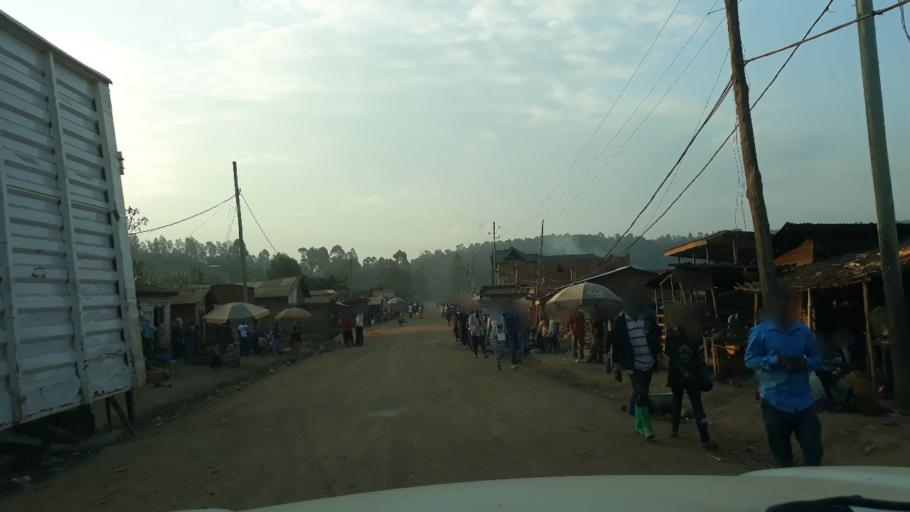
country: CD
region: South Kivu
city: Bukavu
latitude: -2.6601
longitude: 28.8741
